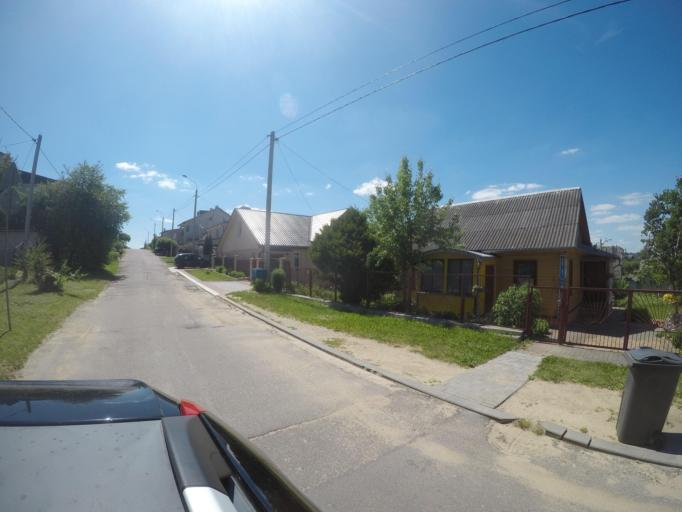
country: BY
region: Grodnenskaya
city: Hrodna
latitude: 53.6937
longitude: 23.8180
